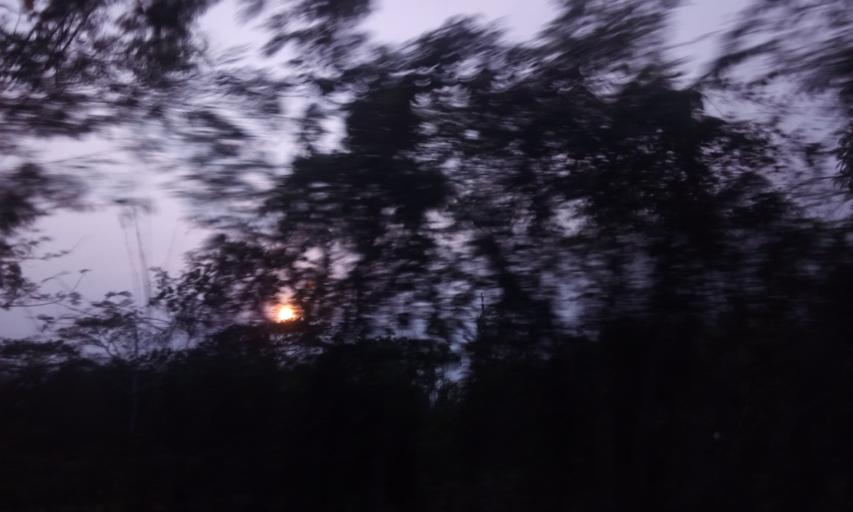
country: TH
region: Bangkok
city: Nong Chok
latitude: 13.9172
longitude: 100.8911
